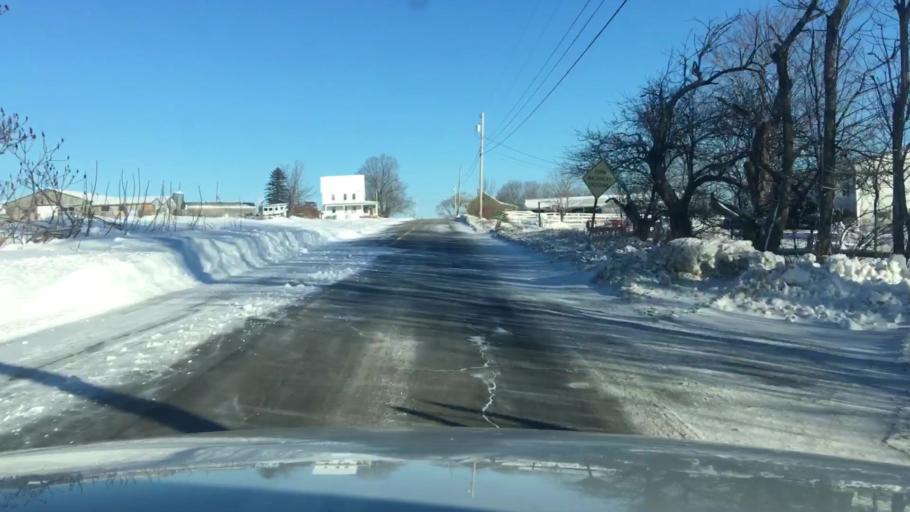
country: US
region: Maine
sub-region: Kennebec County
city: Mount Vernon
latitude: 44.4819
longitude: -69.9724
